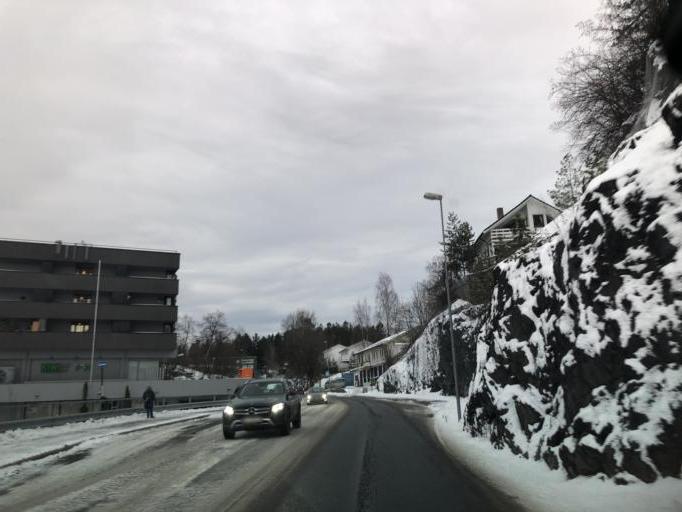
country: NO
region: Akershus
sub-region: Baerum
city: Sandvika
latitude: 59.8714
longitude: 10.5165
